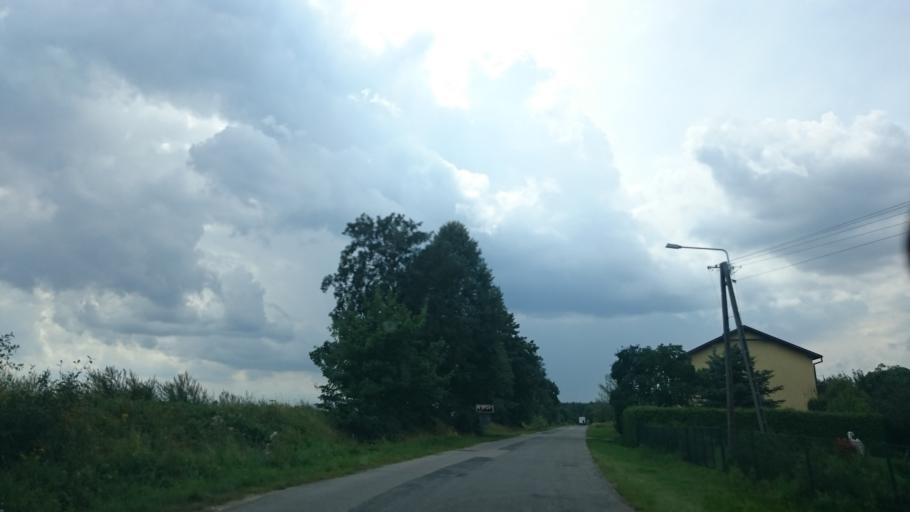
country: PL
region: Pomeranian Voivodeship
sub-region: Powiat chojnicki
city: Chojnice
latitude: 53.6982
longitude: 17.6852
